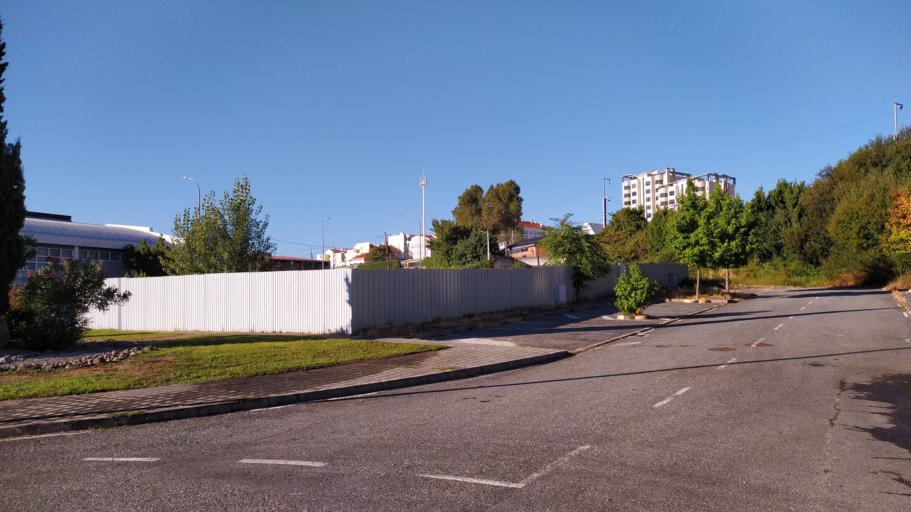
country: PT
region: Castelo Branco
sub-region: Covilha
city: Covilha
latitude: 40.2797
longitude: -7.4954
